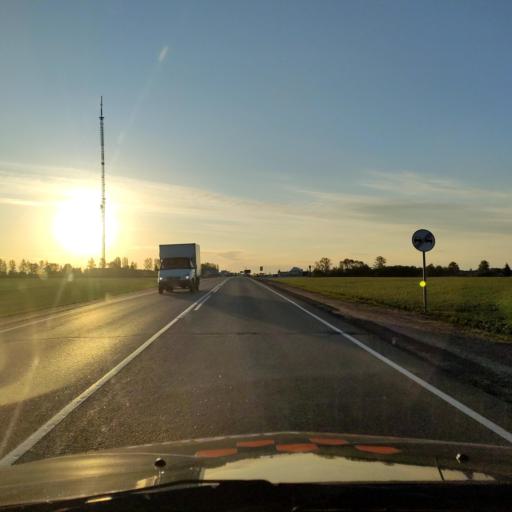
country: RU
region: Orjol
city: Livny
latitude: 52.4490
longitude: 37.4919
